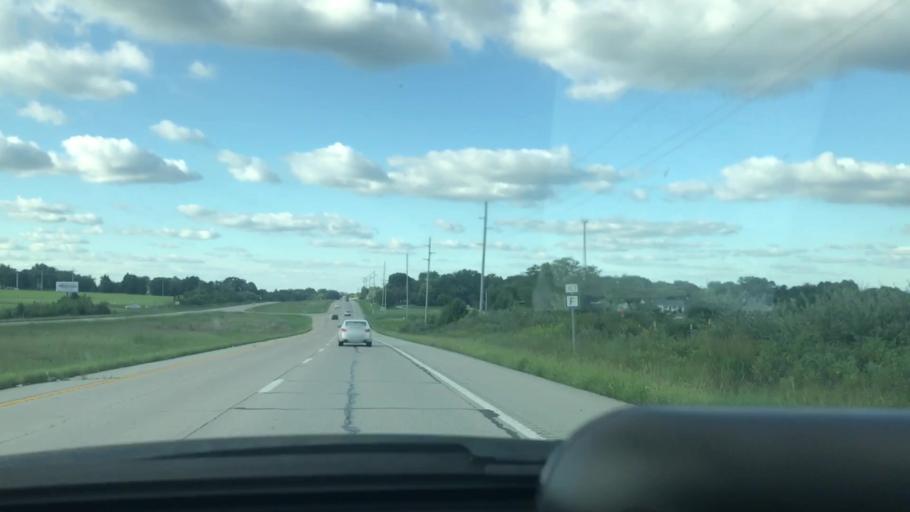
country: US
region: Missouri
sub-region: Pettis County
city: Sedalia
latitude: 38.6236
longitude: -93.2672
